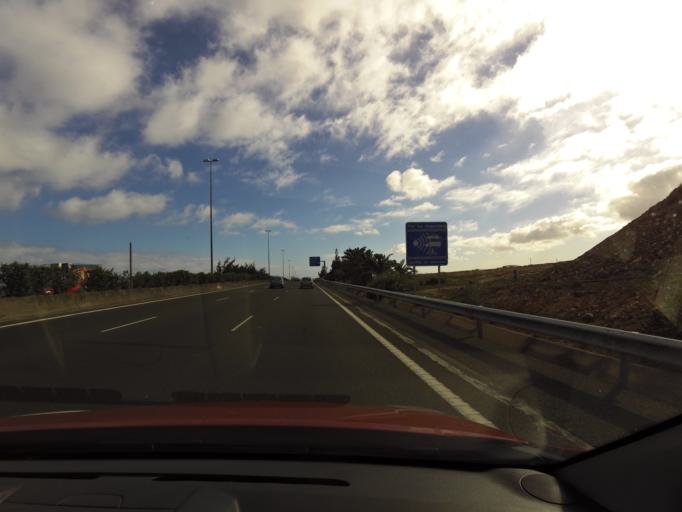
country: ES
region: Canary Islands
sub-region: Provincia de Las Palmas
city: Telde
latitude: 27.9601
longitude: -15.3889
